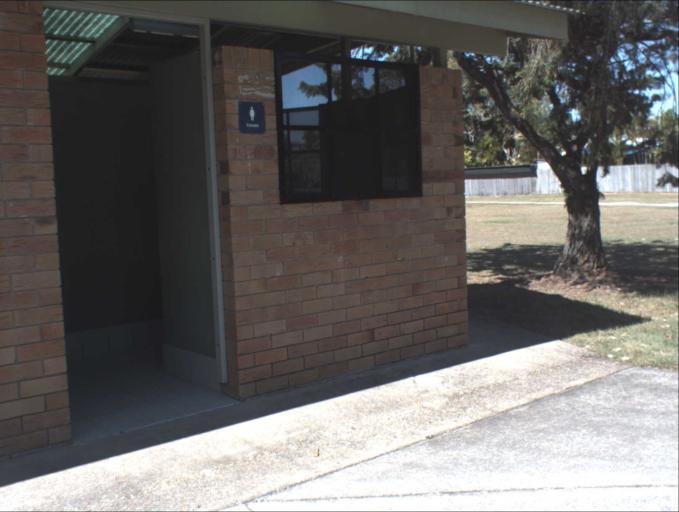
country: AU
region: Queensland
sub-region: Gold Coast
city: Yatala
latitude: -27.7089
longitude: 153.2249
